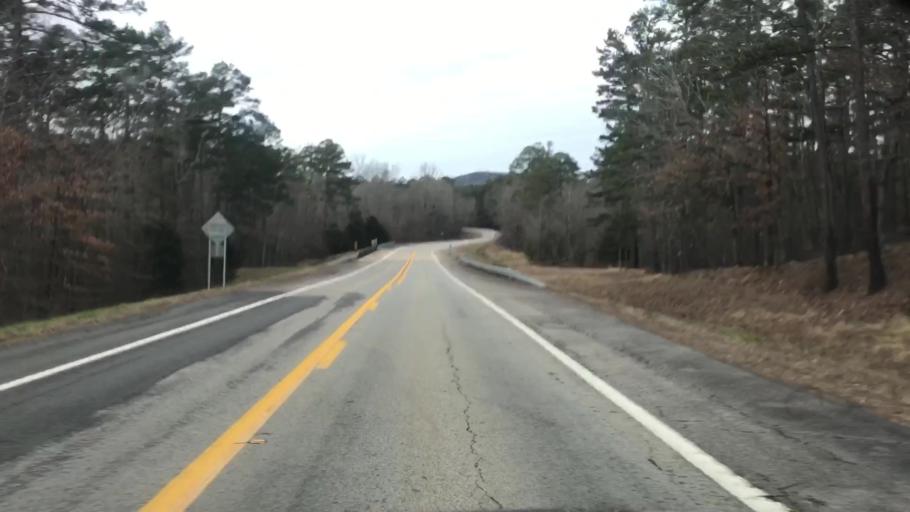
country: US
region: Arkansas
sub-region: Montgomery County
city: Mount Ida
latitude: 34.6848
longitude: -93.8043
